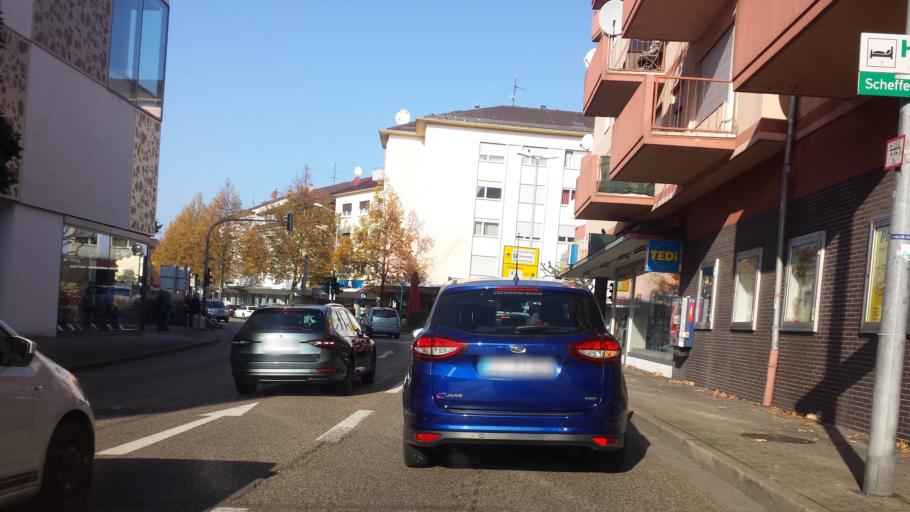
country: DE
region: Baden-Wuerttemberg
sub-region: Karlsruhe Region
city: Bruchsal
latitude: 49.1255
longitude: 8.5981
